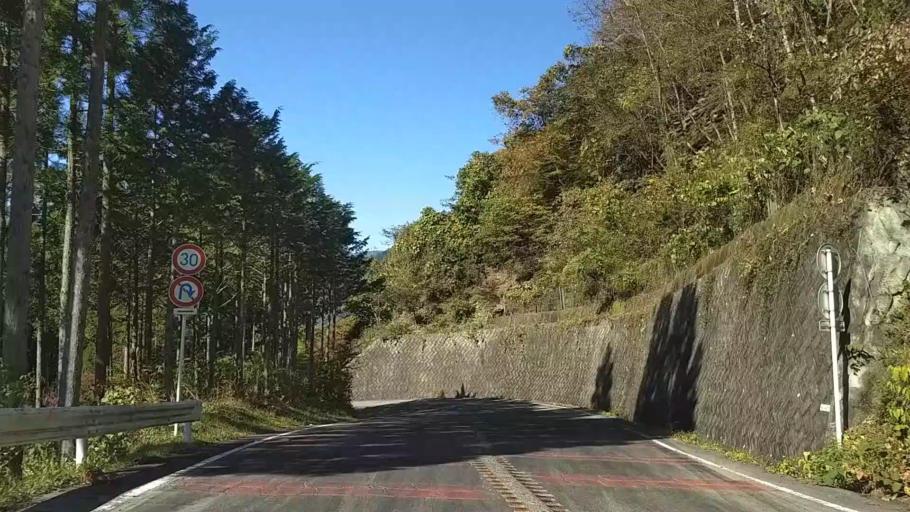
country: JP
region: Yamanashi
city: Otsuki
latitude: 35.7339
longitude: 138.9740
